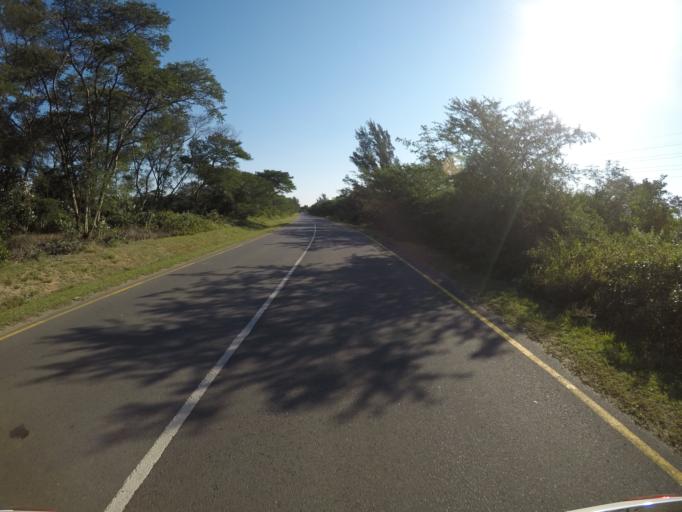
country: ZA
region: KwaZulu-Natal
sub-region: uThungulu District Municipality
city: Richards Bay
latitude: -28.7818
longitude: 32.0720
